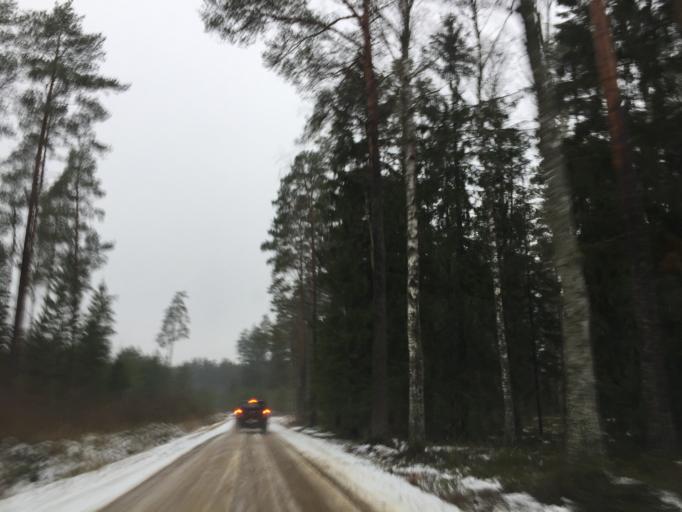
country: LV
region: Seja
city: Loja
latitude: 57.1291
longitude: 24.6074
